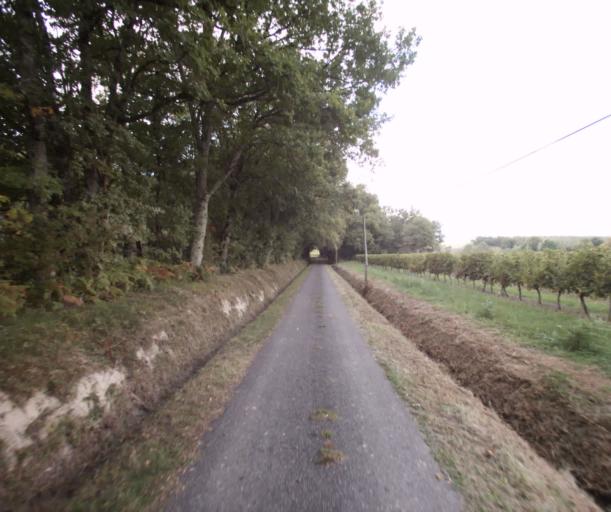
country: FR
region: Midi-Pyrenees
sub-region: Departement du Gers
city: Cazaubon
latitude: 43.8924
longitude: -0.0482
